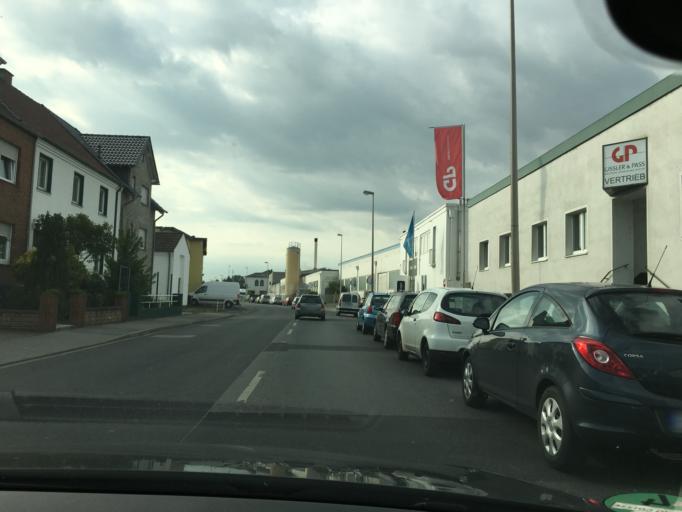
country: DE
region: North Rhine-Westphalia
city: Julich
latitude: 50.9182
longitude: 6.3709
